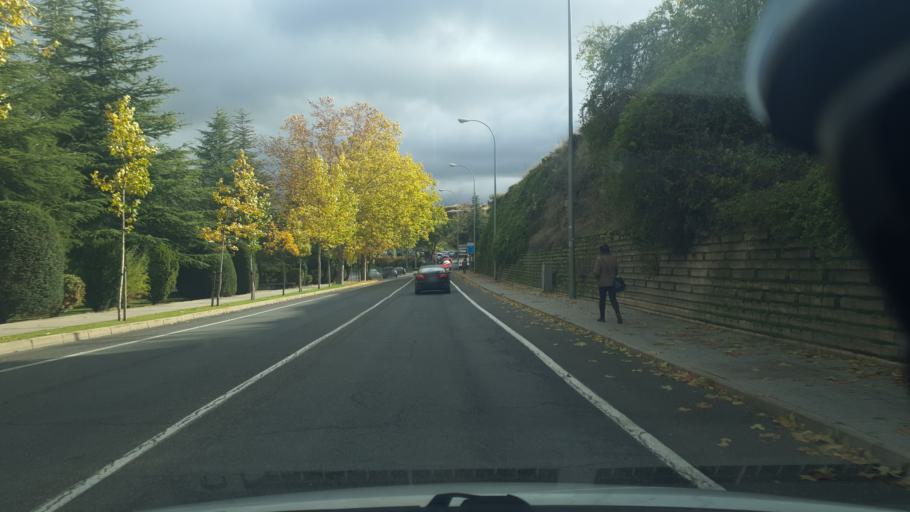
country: ES
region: Castille and Leon
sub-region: Provincia de Segovia
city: Segovia
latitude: 40.9441
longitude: -4.1246
